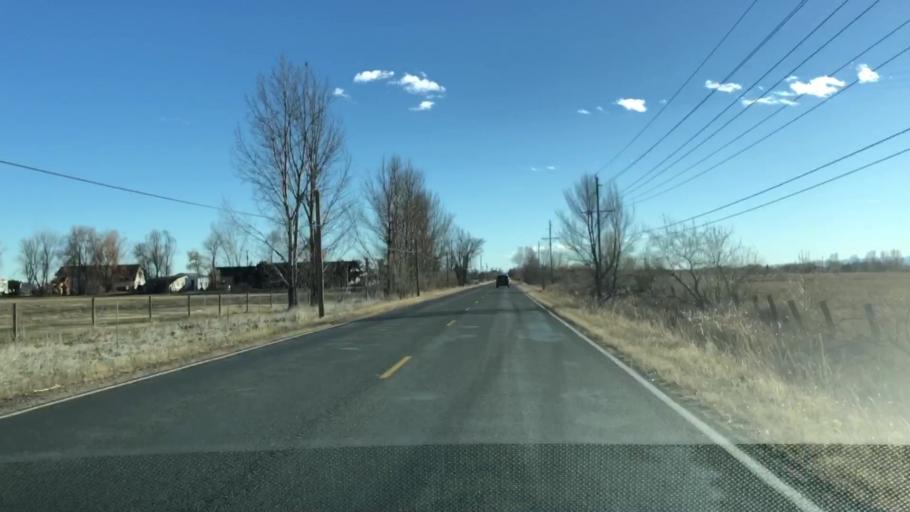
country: US
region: Colorado
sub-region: Weld County
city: Windsor
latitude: 40.5473
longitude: -104.9825
